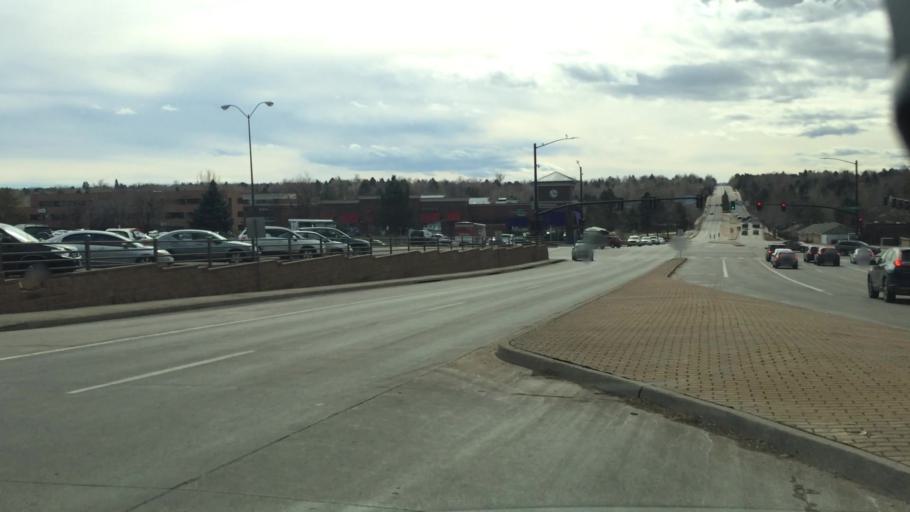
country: US
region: Colorado
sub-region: Arapahoe County
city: Castlewood
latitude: 39.5961
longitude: -104.9042
